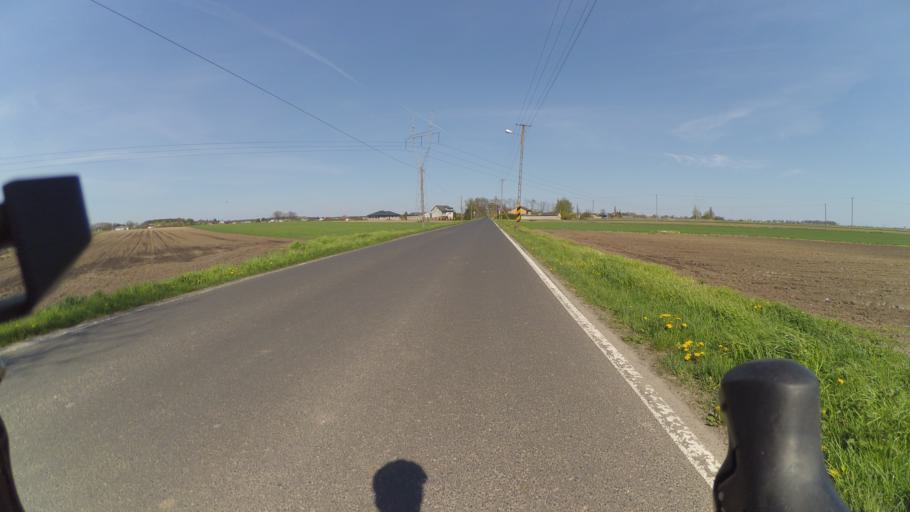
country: PL
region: Masovian Voivodeship
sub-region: Powiat warszawski zachodni
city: Leszno
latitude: 52.2496
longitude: 20.5597
